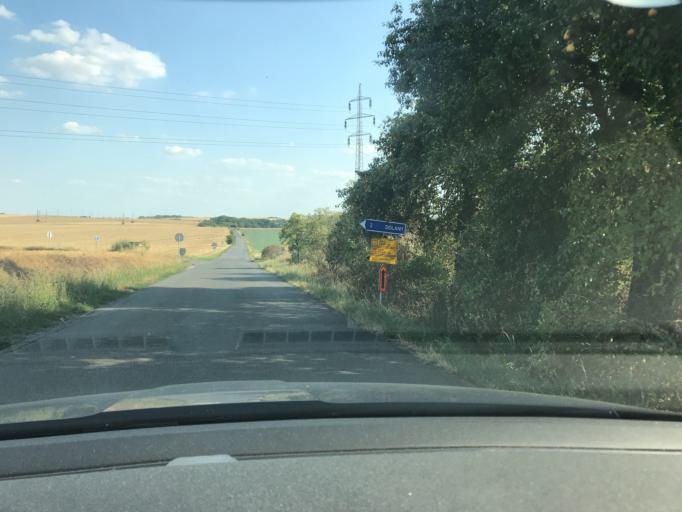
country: CZ
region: Central Bohemia
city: Kralupy nad Vltavou
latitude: 50.2274
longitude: 14.3205
